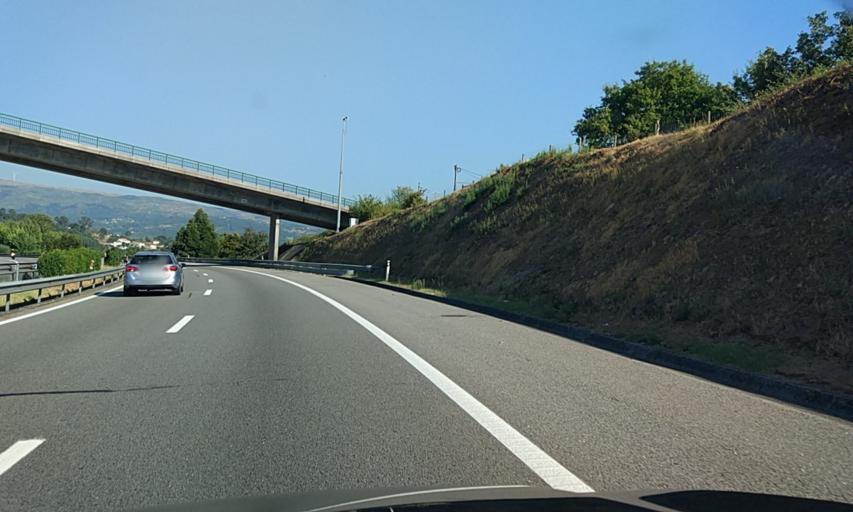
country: PT
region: Porto
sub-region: Marco de Canaveses
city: Marco de Canavezes
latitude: 41.2277
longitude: -8.1647
